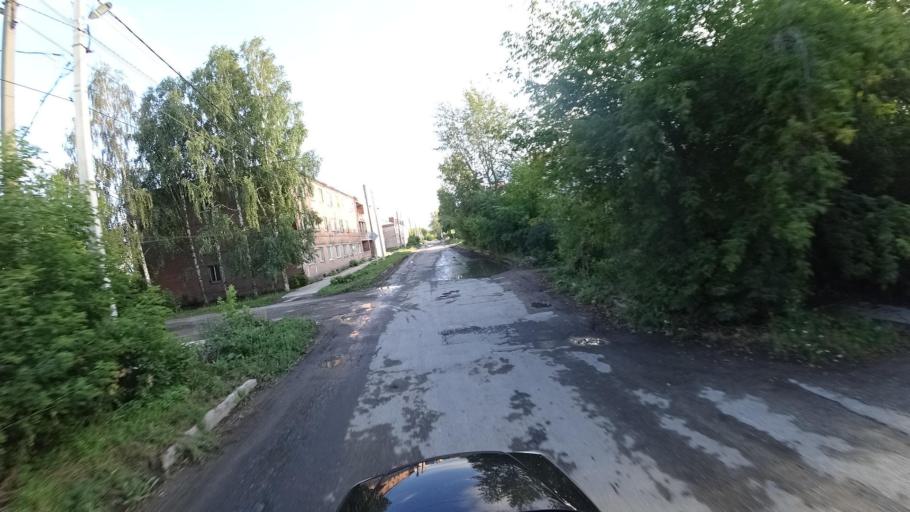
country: RU
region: Sverdlovsk
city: Kamyshlov
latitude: 56.8527
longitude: 62.7283
